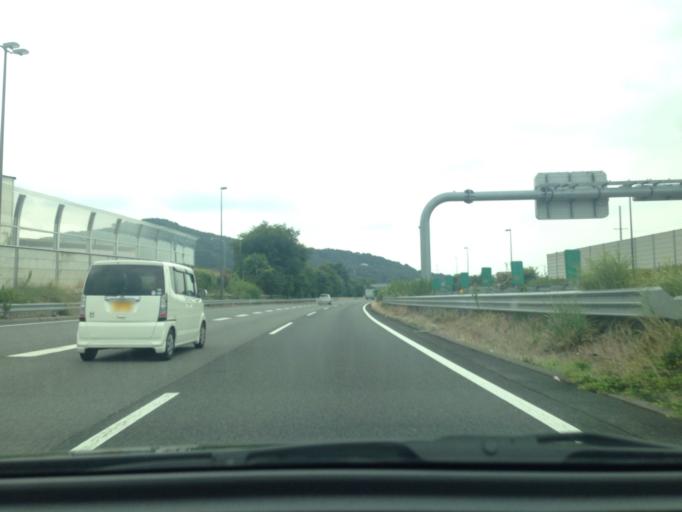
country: JP
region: Aichi
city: Shinshiro
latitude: 34.8220
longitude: 137.5492
